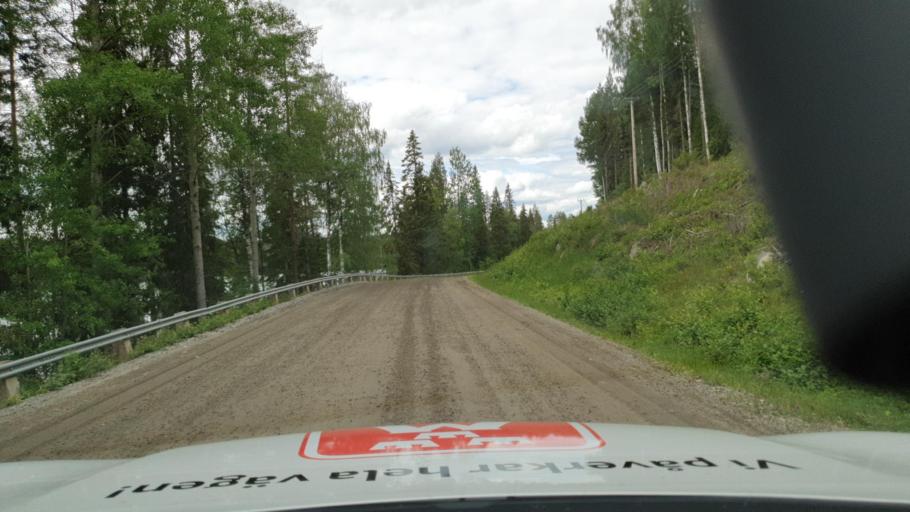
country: SE
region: Vaesterbotten
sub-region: Bjurholms Kommun
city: Bjurholm
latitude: 63.8415
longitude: 18.9928
